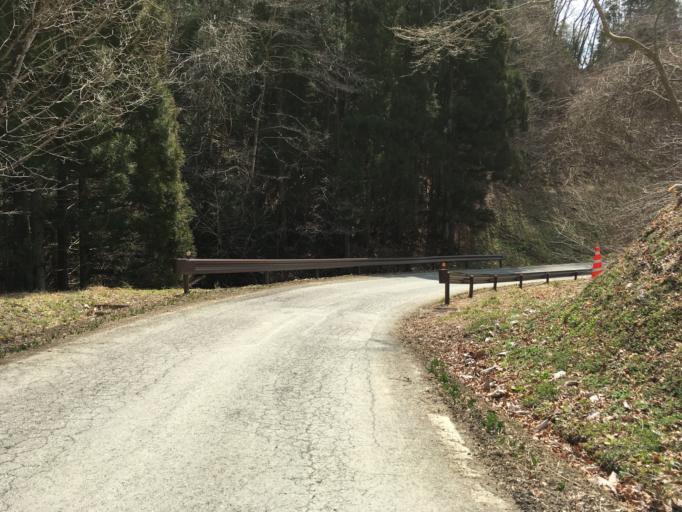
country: JP
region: Iwate
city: Ichinoseki
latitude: 38.8198
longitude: 141.2728
